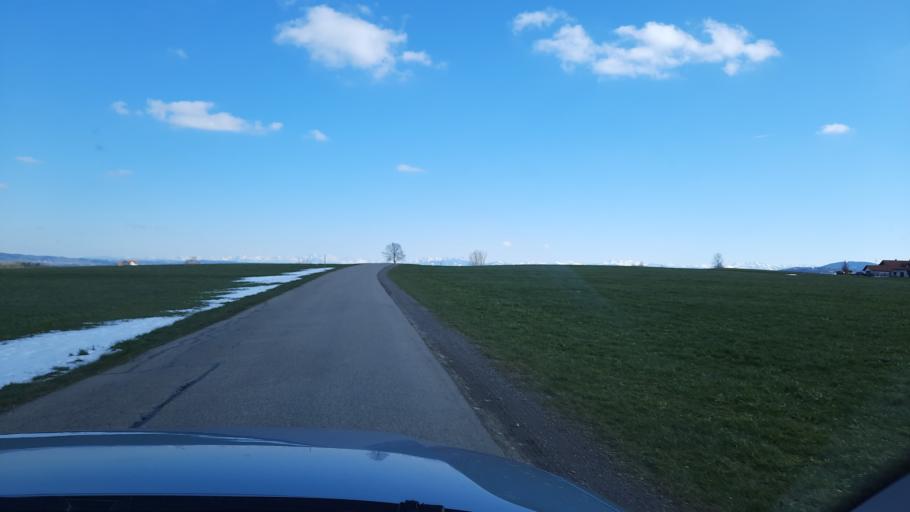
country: DE
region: Bavaria
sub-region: Swabia
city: Altusried
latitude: 47.8169
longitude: 10.2004
